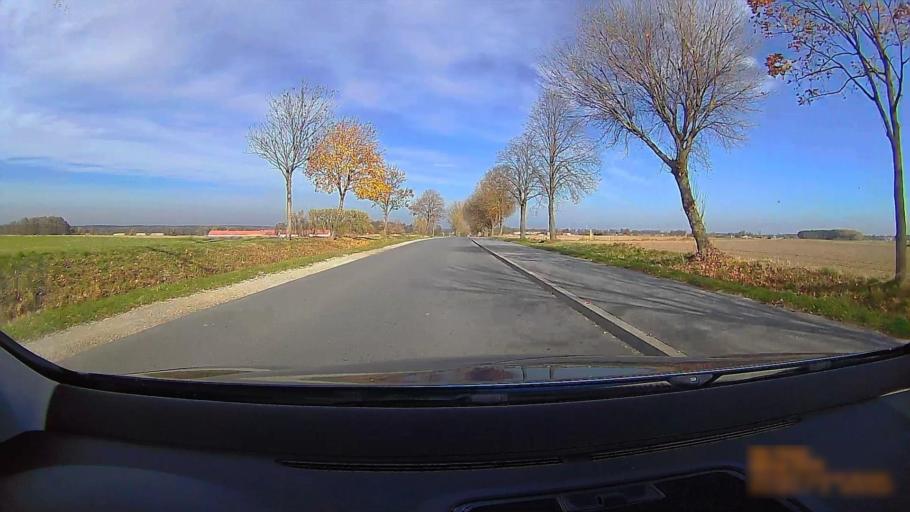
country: PL
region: Greater Poland Voivodeship
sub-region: Powiat kepinski
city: Kepno
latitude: 51.3384
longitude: 18.0211
